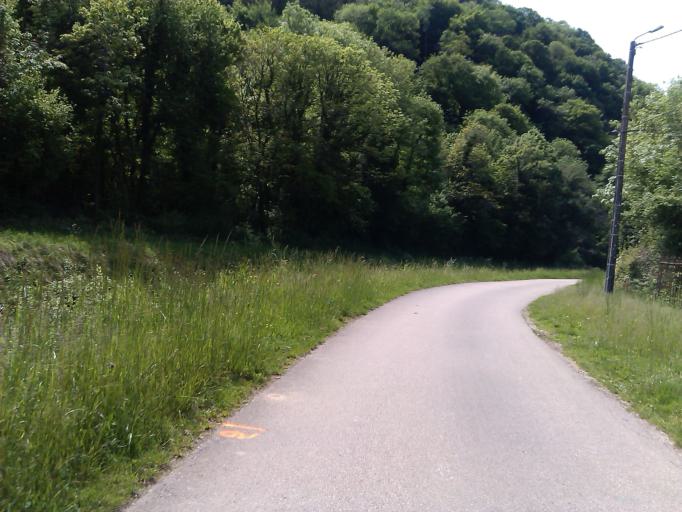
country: FR
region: Franche-Comte
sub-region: Departement du Doubs
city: Montferrand-le-Chateau
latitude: 47.1698
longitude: 5.9136
